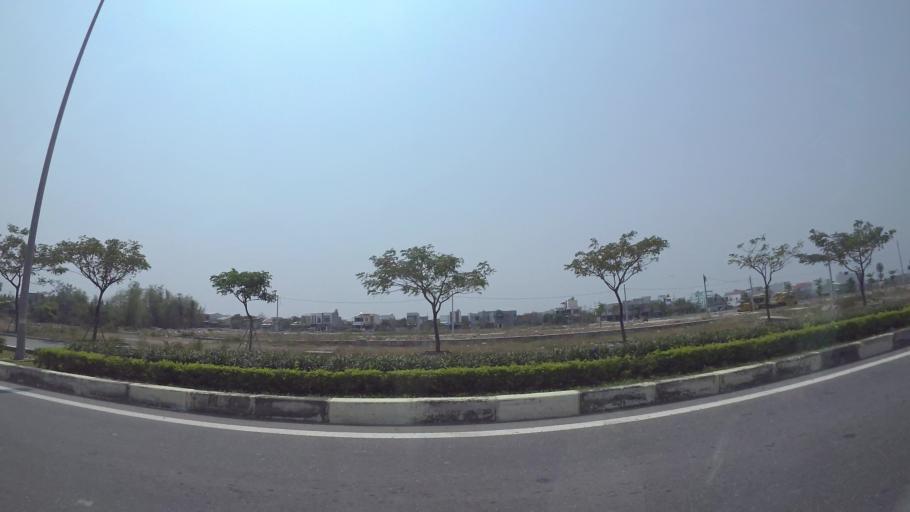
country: VN
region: Da Nang
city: Ngu Hanh Son
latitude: 15.9882
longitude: 108.2396
